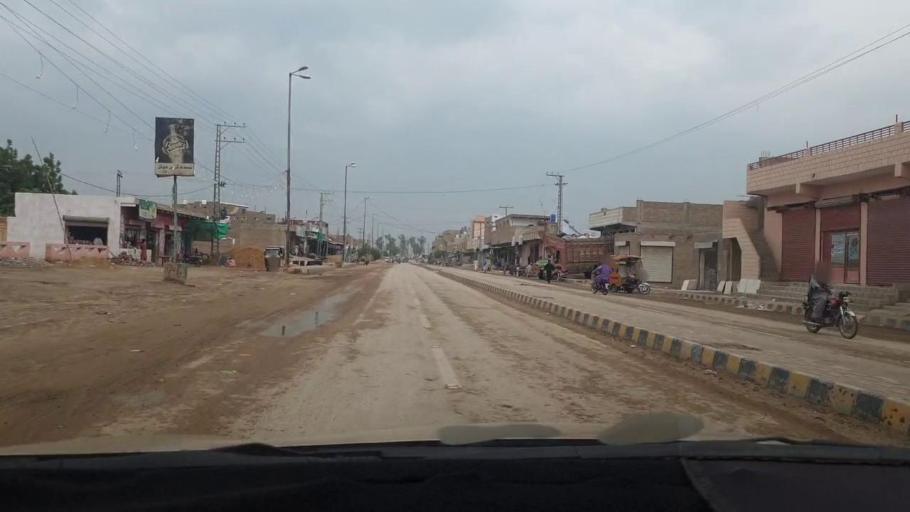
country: PK
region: Sindh
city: Larkana
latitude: 27.5749
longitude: 68.2283
